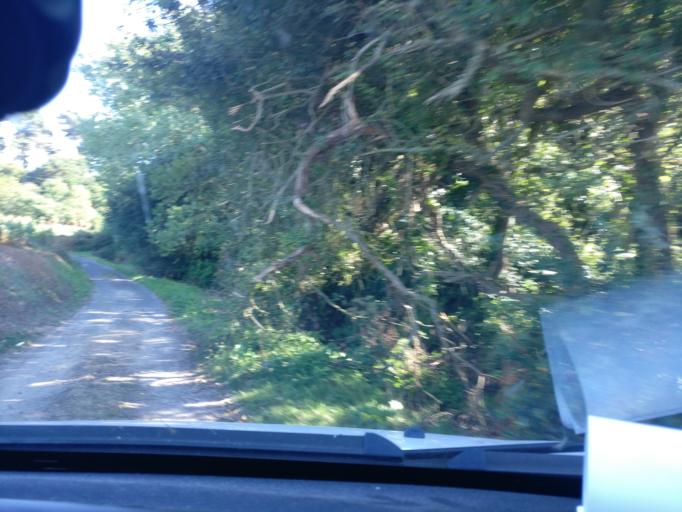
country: FR
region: Brittany
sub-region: Departement des Cotes-d'Armor
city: Trelevern
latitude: 48.8185
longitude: -3.3658
